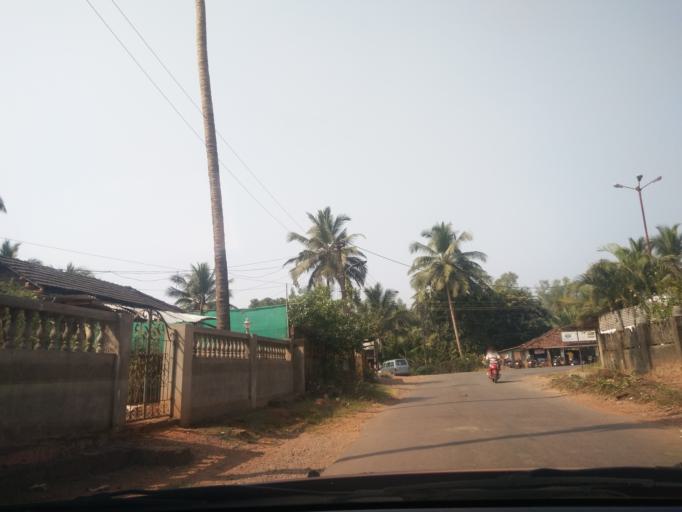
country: IN
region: Goa
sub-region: North Goa
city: Valpoy
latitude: 15.5030
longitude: 74.1361
